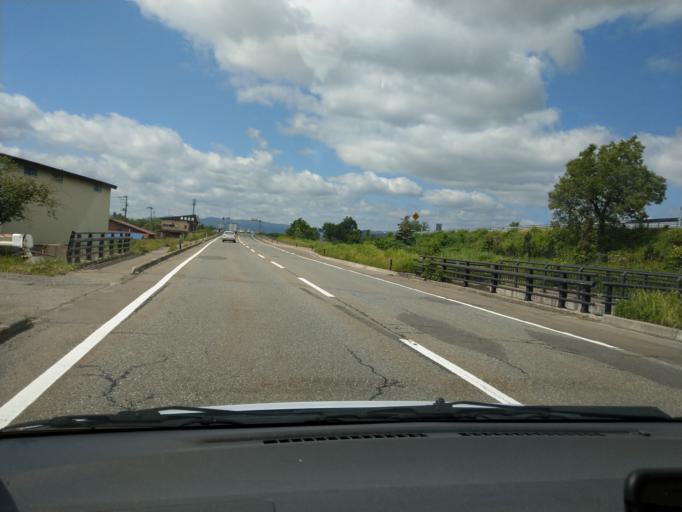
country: JP
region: Akita
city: Yuzawa
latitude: 39.2128
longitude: 140.5131
